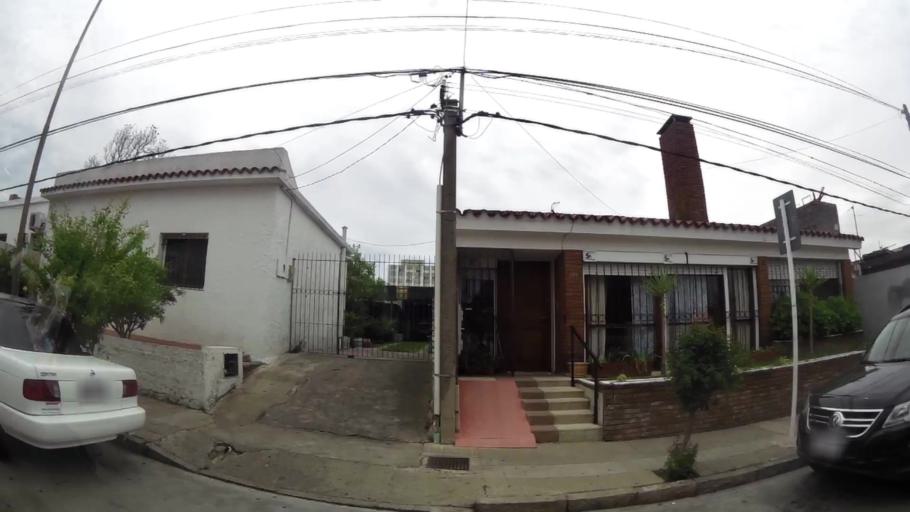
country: UY
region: Maldonado
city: Maldonado
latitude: -34.9058
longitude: -54.9556
